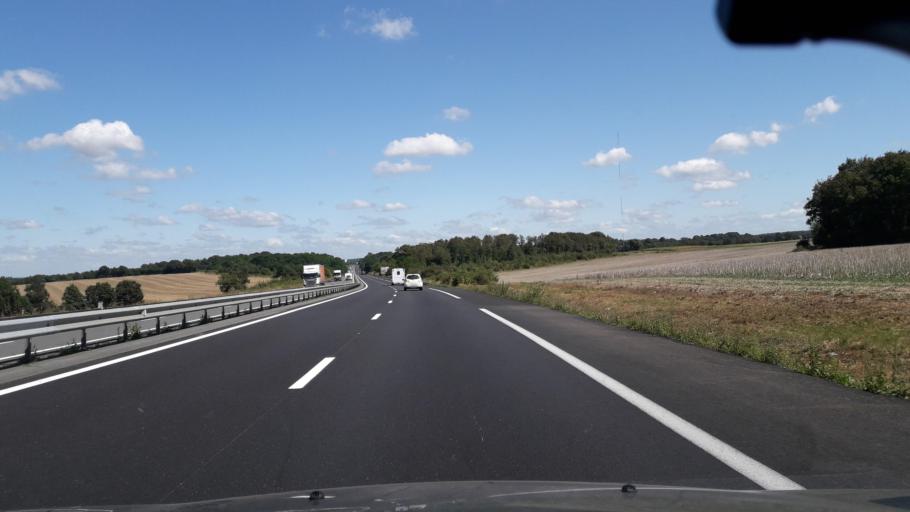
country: FR
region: Poitou-Charentes
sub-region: Departement de la Charente
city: Chasseneuil-sur-Bonnieure
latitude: 45.7956
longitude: 0.4332
